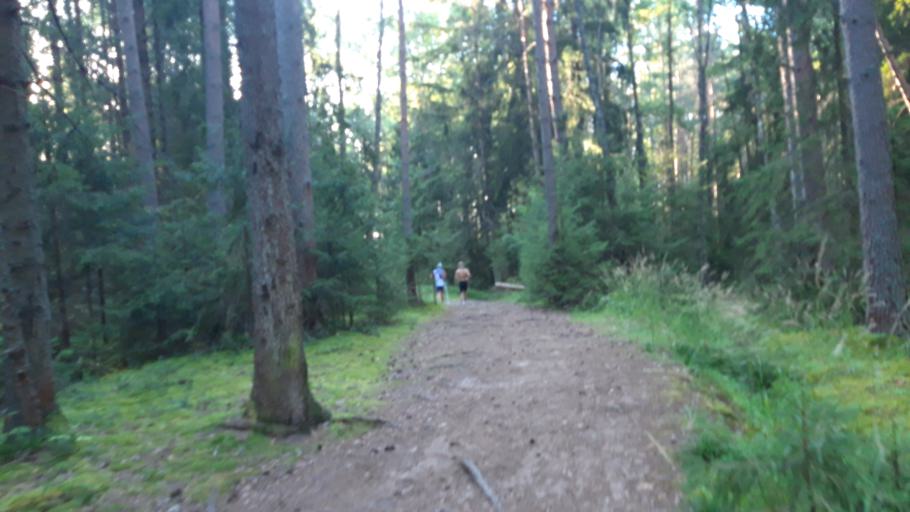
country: RU
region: Tverskaya
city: Konakovo
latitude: 56.6740
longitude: 36.6901
